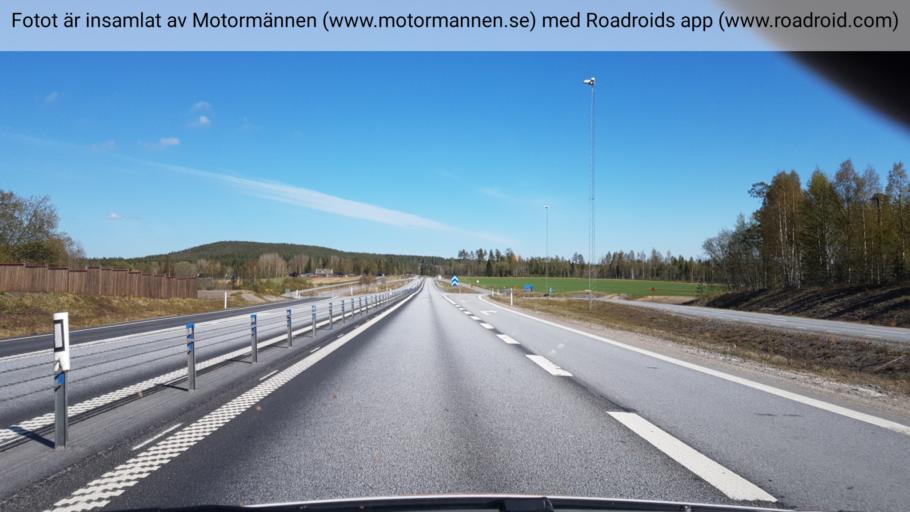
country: SE
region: Vaesterbotten
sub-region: Vannas Kommun
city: Vannasby
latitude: 63.8940
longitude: 19.9468
